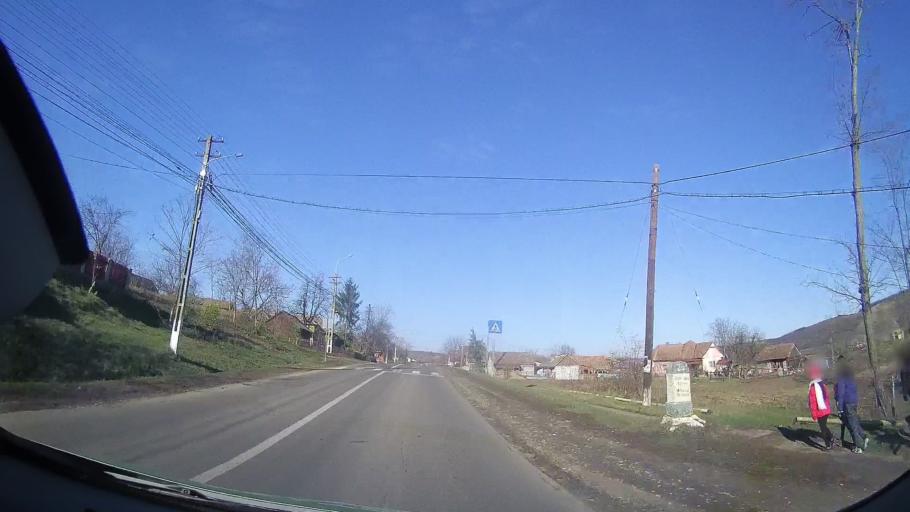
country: RO
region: Mures
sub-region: Comuna Mihesu de Campie
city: Mihesu de Campie
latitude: 46.6746
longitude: 24.1561
